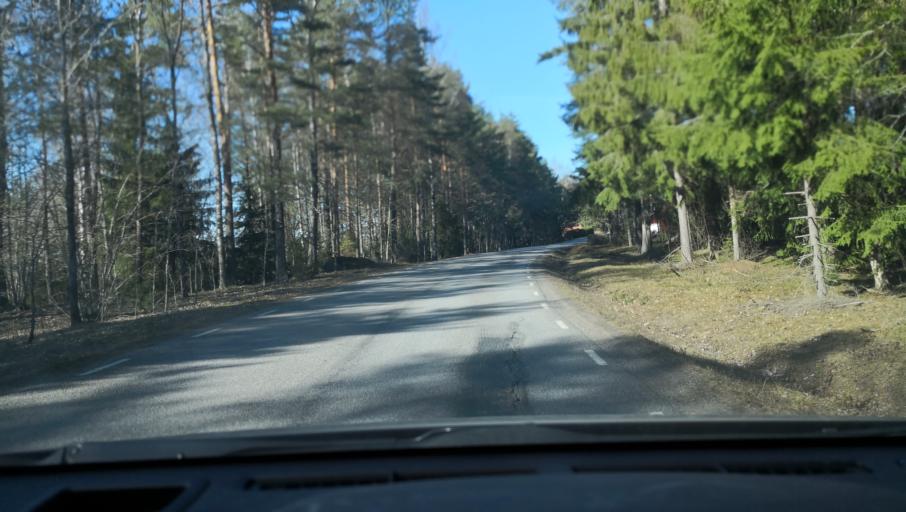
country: SE
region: Vaestmanland
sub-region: Sala Kommun
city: Sala
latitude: 60.0361
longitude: 16.5160
